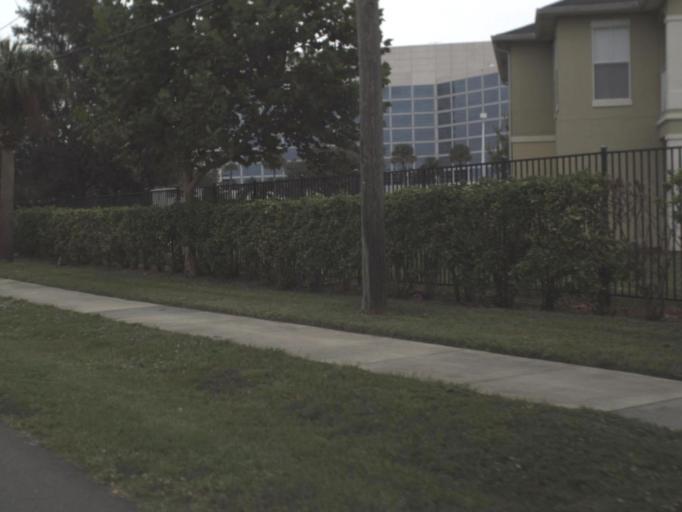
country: US
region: Florida
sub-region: Brevard County
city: Melbourne
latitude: 28.0888
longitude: -80.6270
